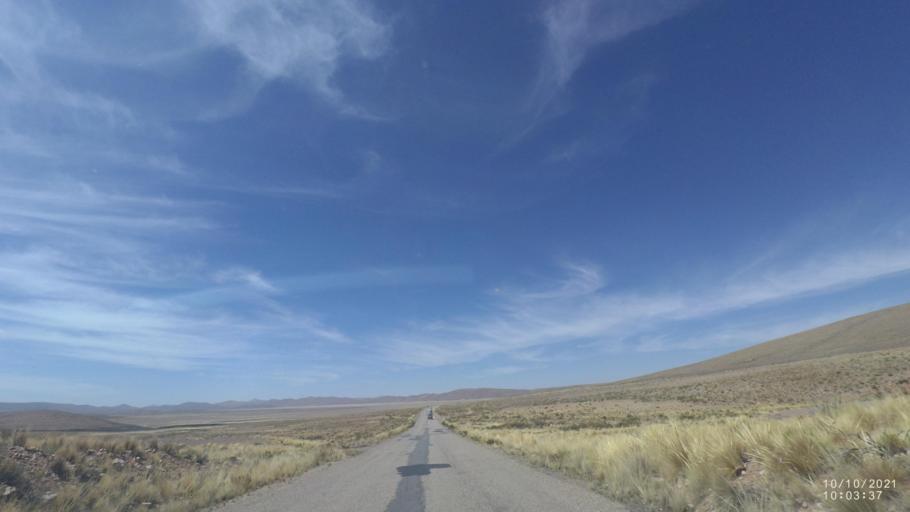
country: BO
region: La Paz
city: Eucaliptus
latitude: -17.3720
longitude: -67.4410
